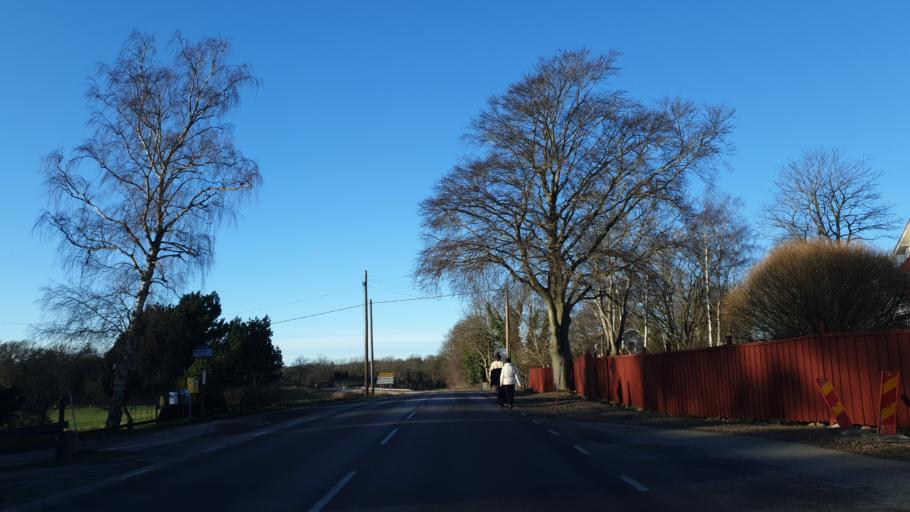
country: SE
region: Blekinge
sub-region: Ronneby Kommun
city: Ronneby
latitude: 56.1971
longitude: 15.3315
